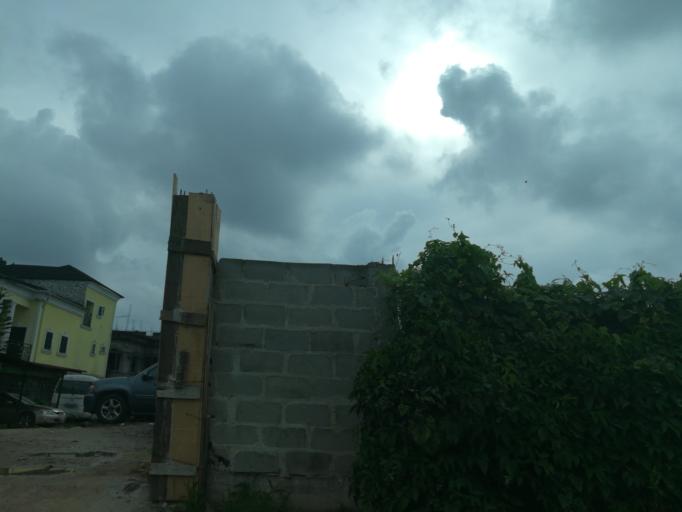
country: NG
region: Rivers
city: Port Harcourt
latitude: 4.8113
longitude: 6.9906
